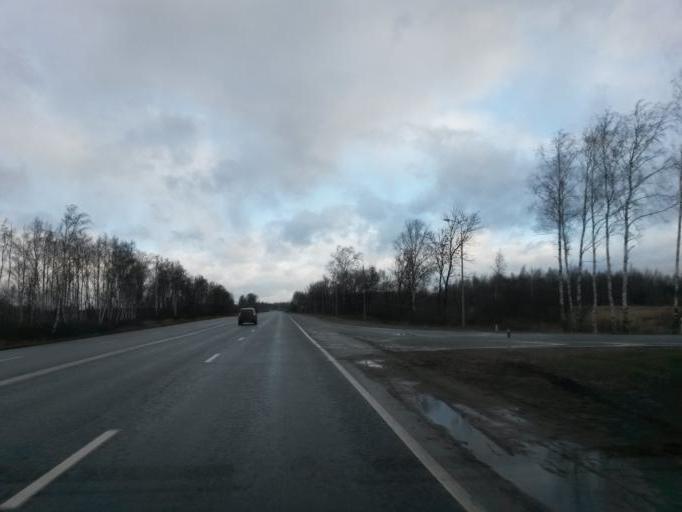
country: RU
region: Jaroslavl
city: Petrovsk
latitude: 57.0479
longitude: 39.2938
